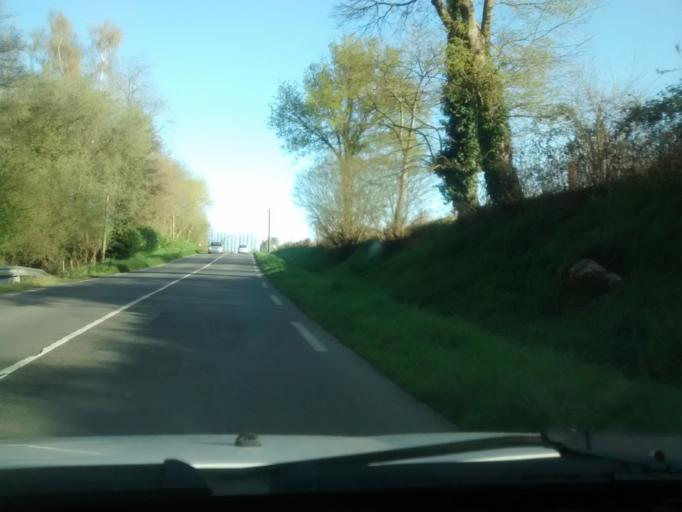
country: FR
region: Brittany
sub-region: Departement d'Ille-et-Vilaine
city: Pleine-Fougeres
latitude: 48.4920
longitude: -1.5819
